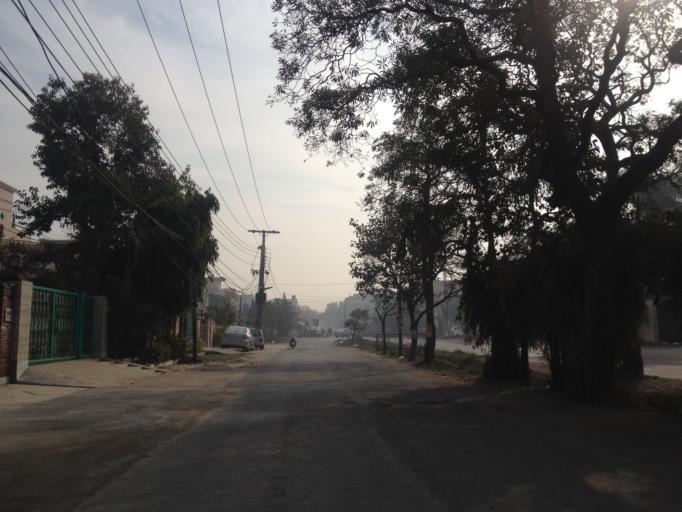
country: PK
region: Punjab
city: Lahore
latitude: 31.4669
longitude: 74.3047
